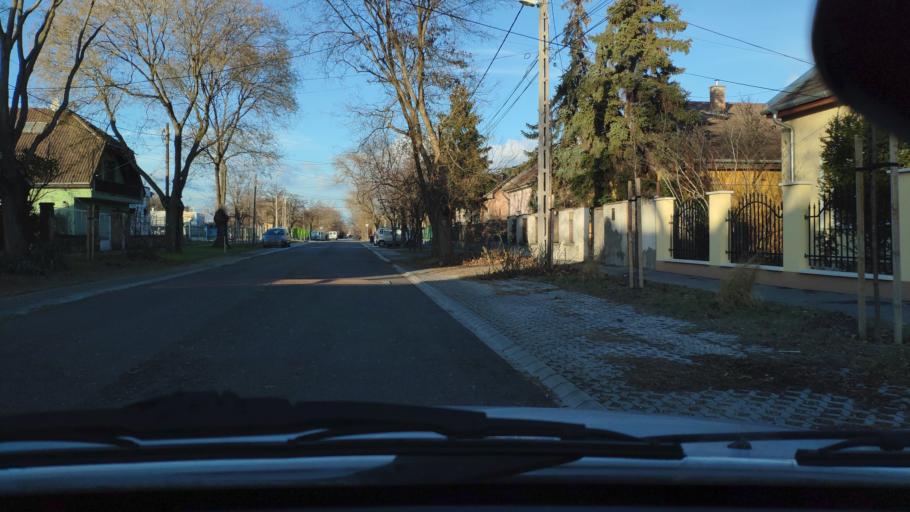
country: HU
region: Budapest
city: Budapest XXI. keruelet
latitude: 47.4215
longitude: 19.0809
